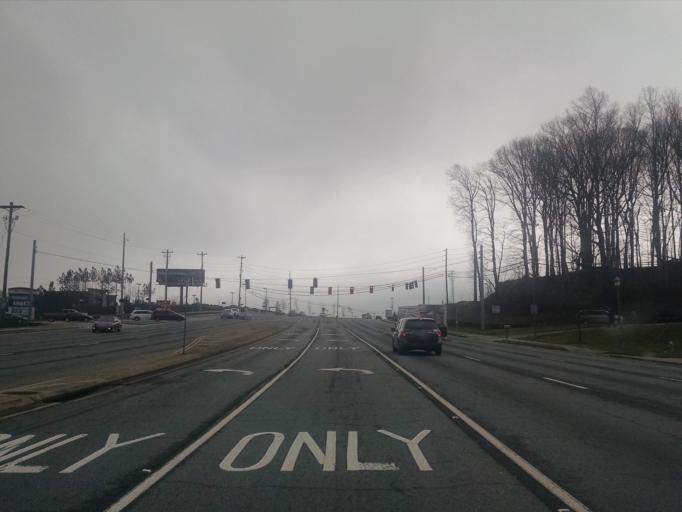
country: US
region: Georgia
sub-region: Gwinnett County
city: Buford
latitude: 34.0855
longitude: -83.9912
